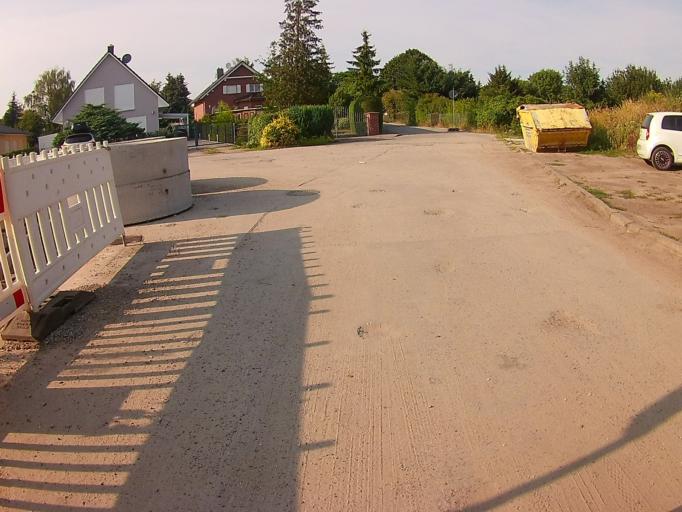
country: DE
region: Berlin
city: Kaulsdorf
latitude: 52.5039
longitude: 13.5776
